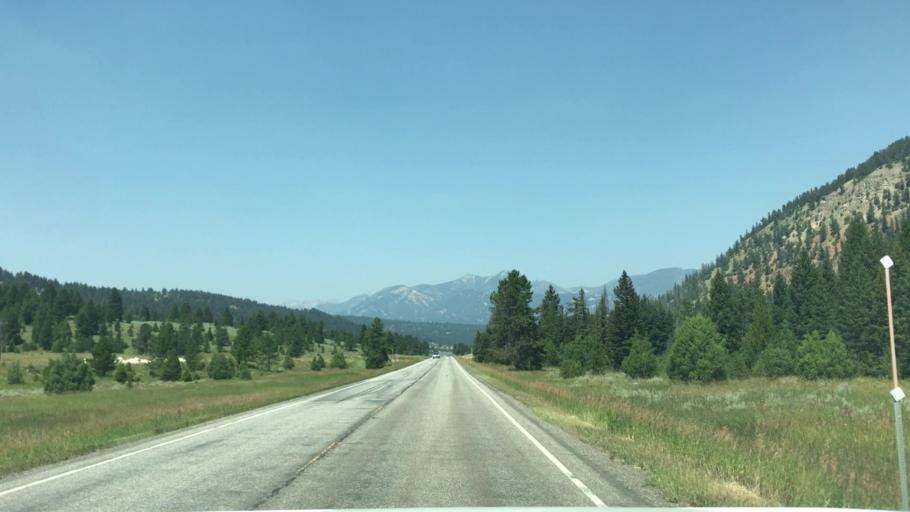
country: US
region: Montana
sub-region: Gallatin County
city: Big Sky
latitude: 45.2015
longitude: -111.2396
